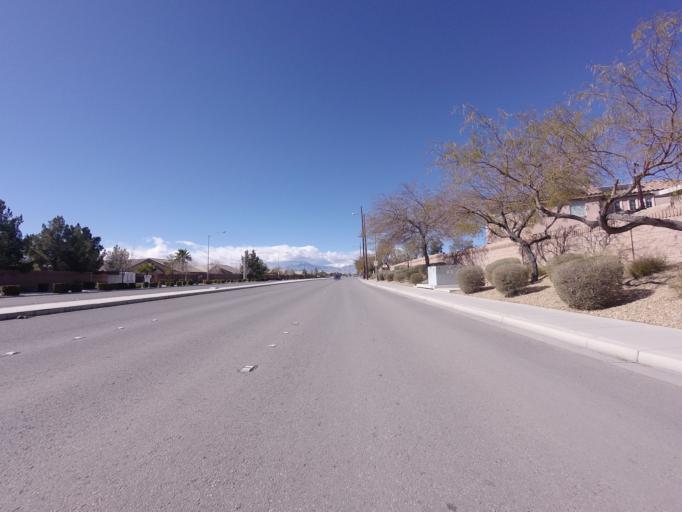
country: US
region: Nevada
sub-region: Clark County
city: Nellis Air Force Base
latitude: 36.2693
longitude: -115.0935
